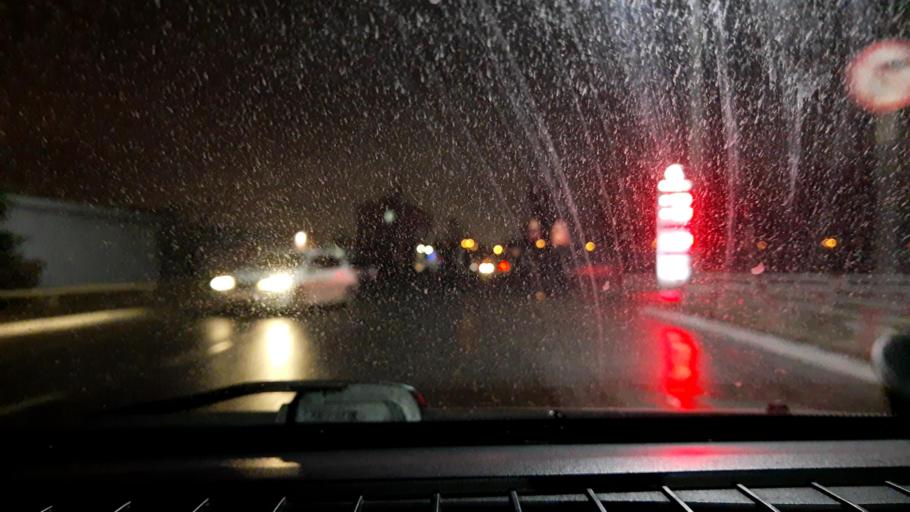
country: RU
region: Nizjnij Novgorod
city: Gorbatovka
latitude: 56.3004
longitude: 43.8712
